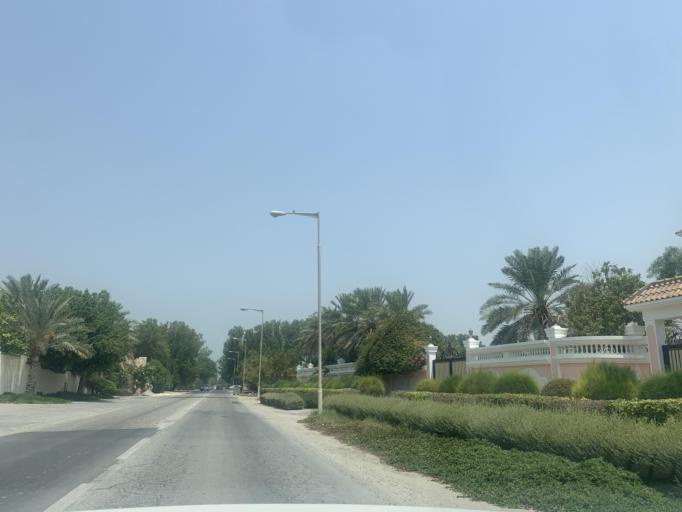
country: BH
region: Central Governorate
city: Madinat Hamad
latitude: 26.1511
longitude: 50.4646
